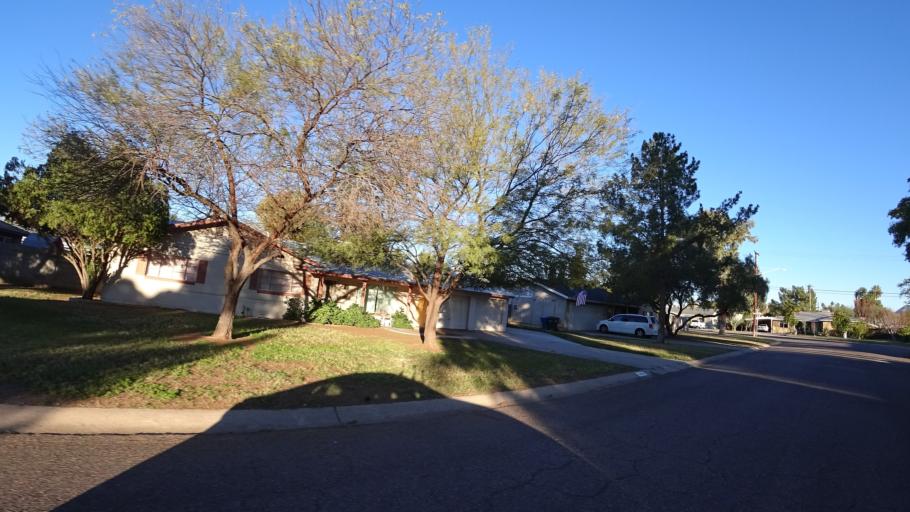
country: US
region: Arizona
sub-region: Maricopa County
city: Paradise Valley
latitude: 33.4925
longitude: -112.0051
